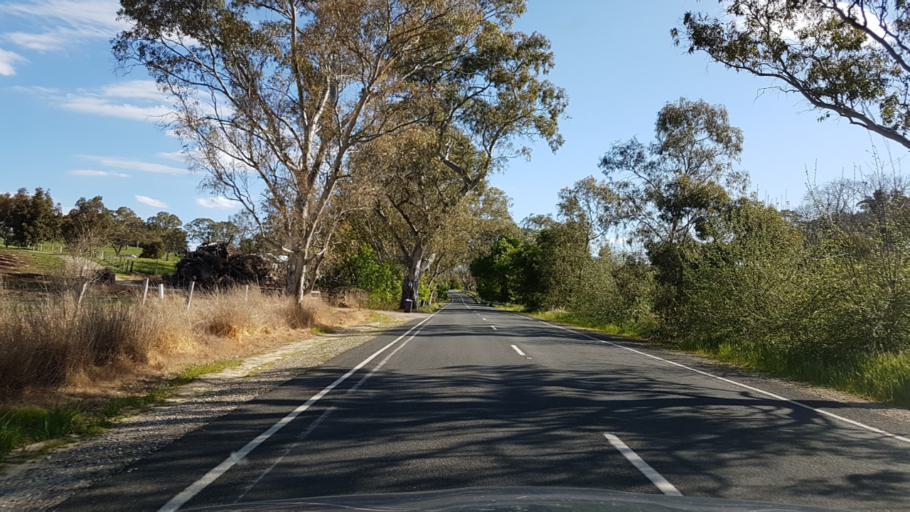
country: AU
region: South Australia
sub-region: Adelaide Hills
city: Gumeracha
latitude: -34.8618
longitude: 138.8919
